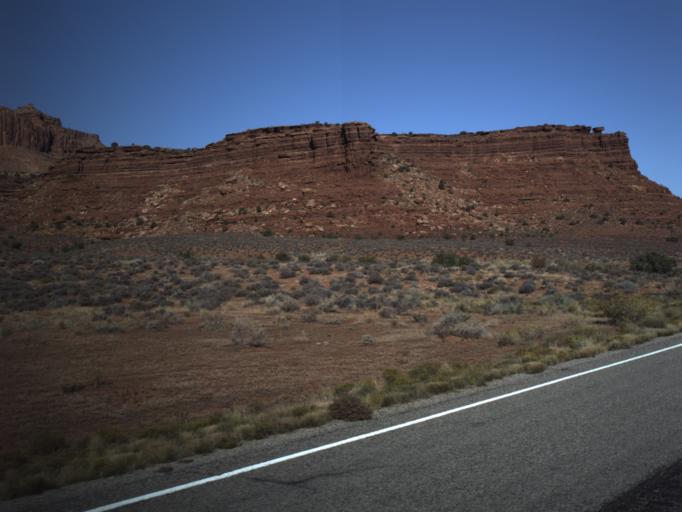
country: US
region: Utah
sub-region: San Juan County
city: Blanding
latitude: 37.7708
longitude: -110.2873
